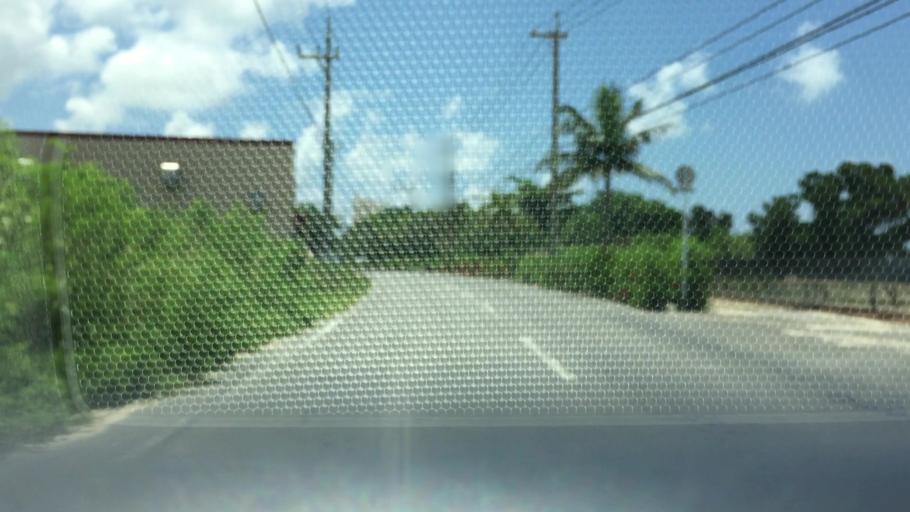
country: JP
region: Okinawa
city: Ishigaki
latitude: 24.3609
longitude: 124.1193
